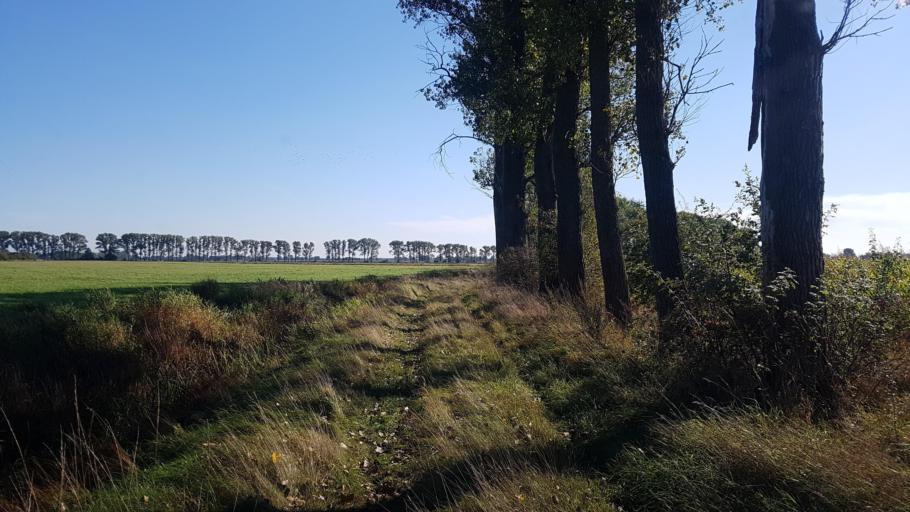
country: DE
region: Brandenburg
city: Plessa
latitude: 51.4634
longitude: 13.5742
